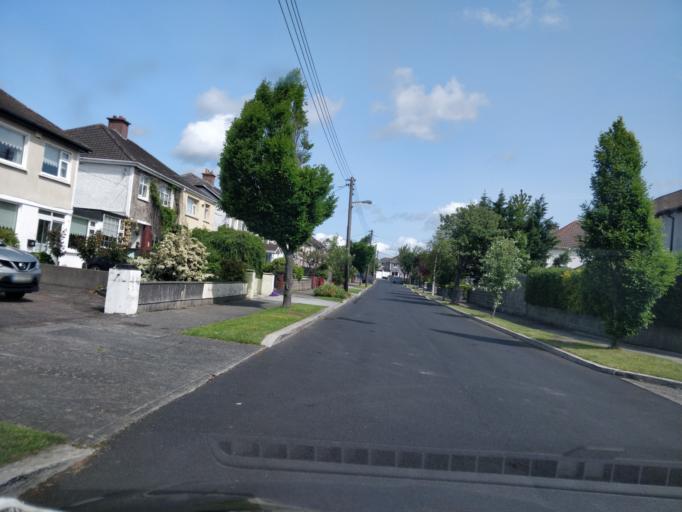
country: IE
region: Leinster
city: Dundrum
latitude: 53.2843
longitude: -6.2543
